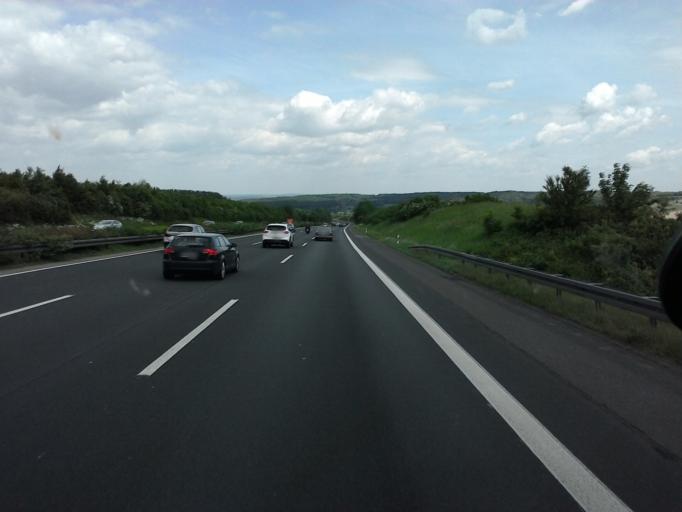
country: DE
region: North Rhine-Westphalia
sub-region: Regierungsbezirk Koln
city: Stossdorf
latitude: 50.7297
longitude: 7.2388
